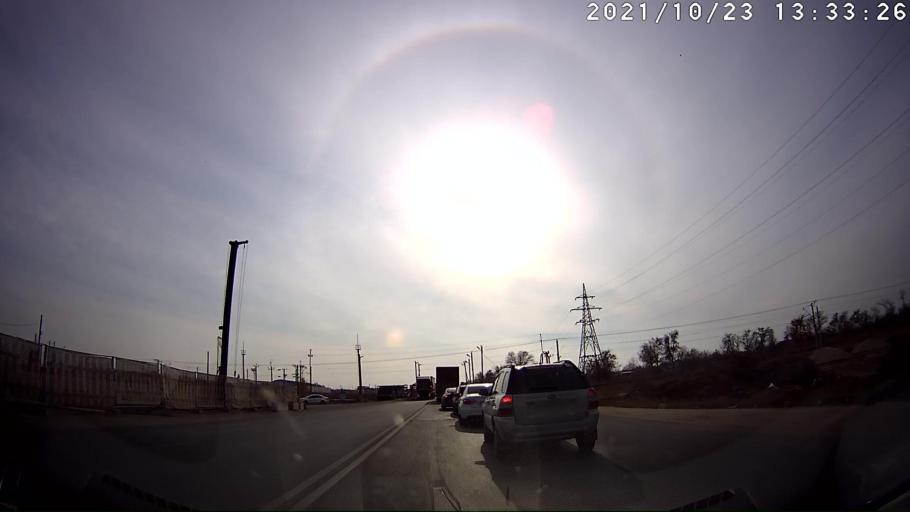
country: RU
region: Volgograd
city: Vodstroy
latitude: 48.8611
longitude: 44.5643
